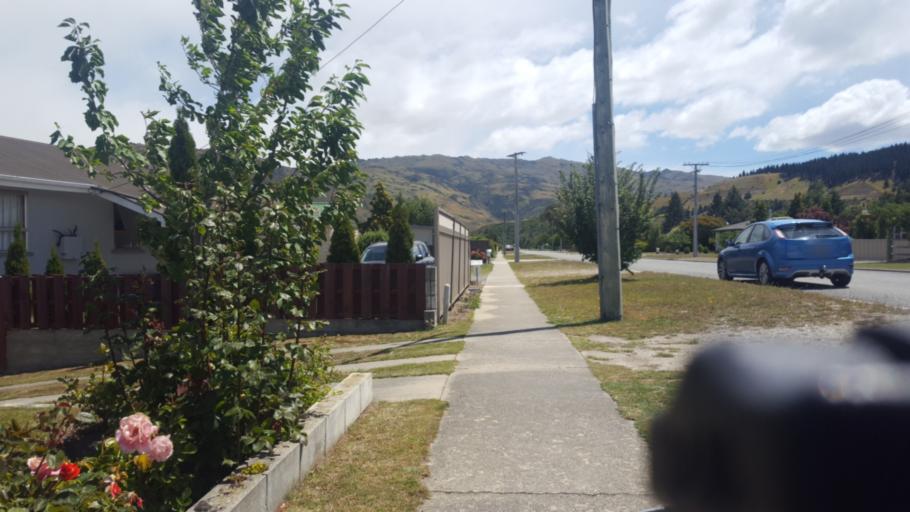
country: NZ
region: Otago
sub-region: Queenstown-Lakes District
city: Wanaka
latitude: -45.1936
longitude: 169.3272
